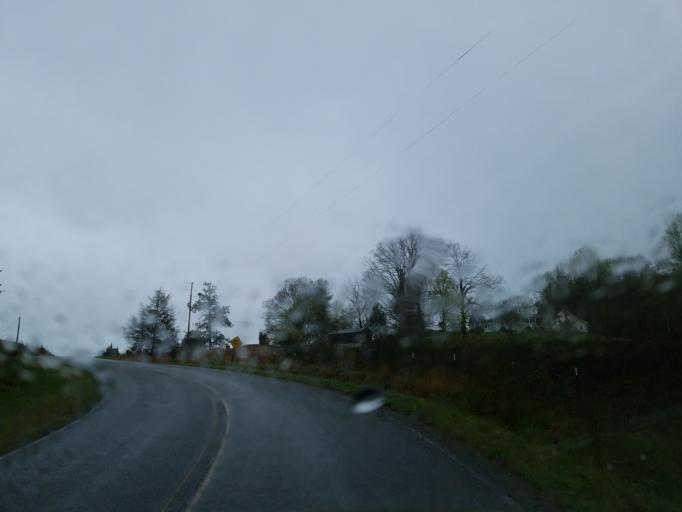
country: US
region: Georgia
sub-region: Fannin County
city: Blue Ridge
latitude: 34.8490
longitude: -84.2299
